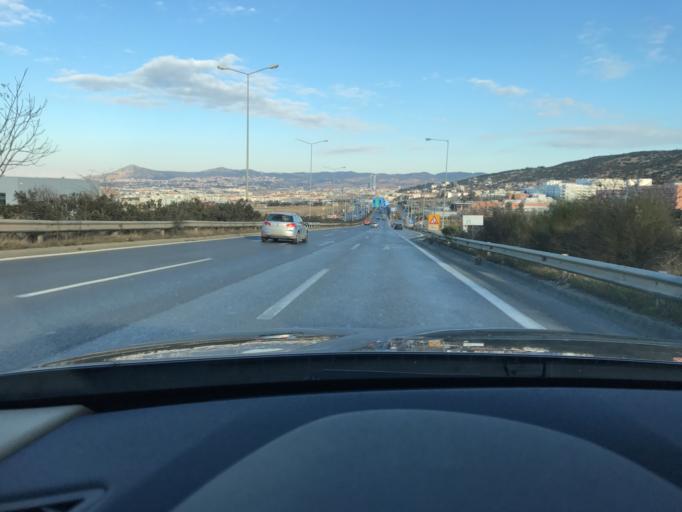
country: GR
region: Central Macedonia
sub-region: Nomos Thessalonikis
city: Polichni
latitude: 40.6685
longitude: 22.9623
